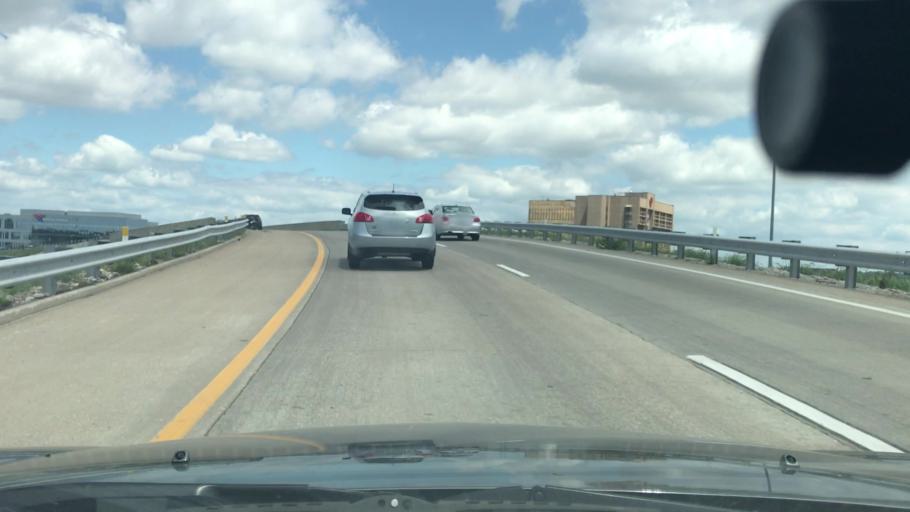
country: US
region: Missouri
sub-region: Saint Louis County
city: Maryland Heights
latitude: 38.6977
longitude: -90.4481
